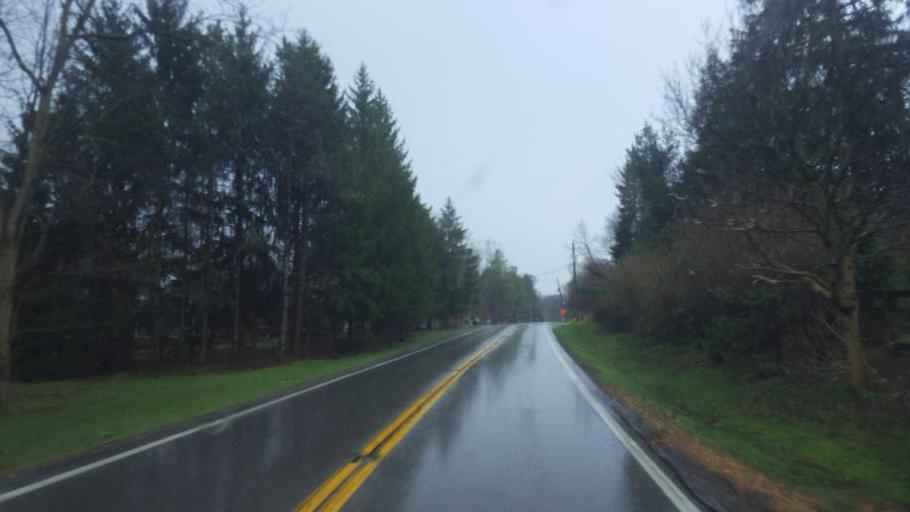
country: US
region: Ohio
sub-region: Delaware County
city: Powell
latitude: 40.1683
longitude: -83.0434
